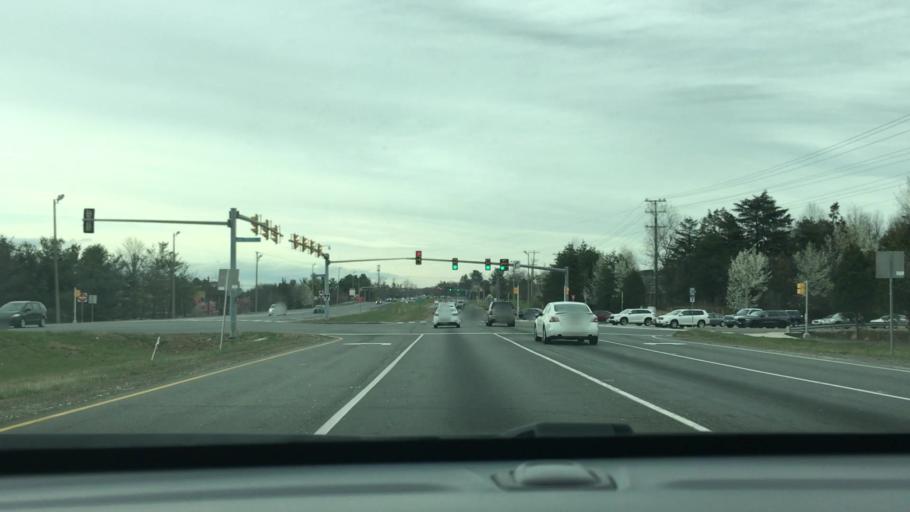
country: US
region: Virginia
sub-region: Fairfax County
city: Centreville
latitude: 38.8269
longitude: -77.4368
